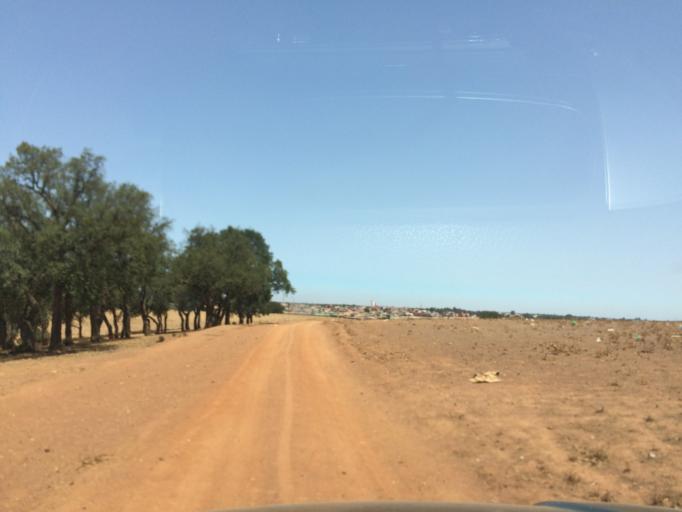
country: MA
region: Chaouia-Ouardigha
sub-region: Benslimane
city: Mellila
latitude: 33.5518
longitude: -6.8954
